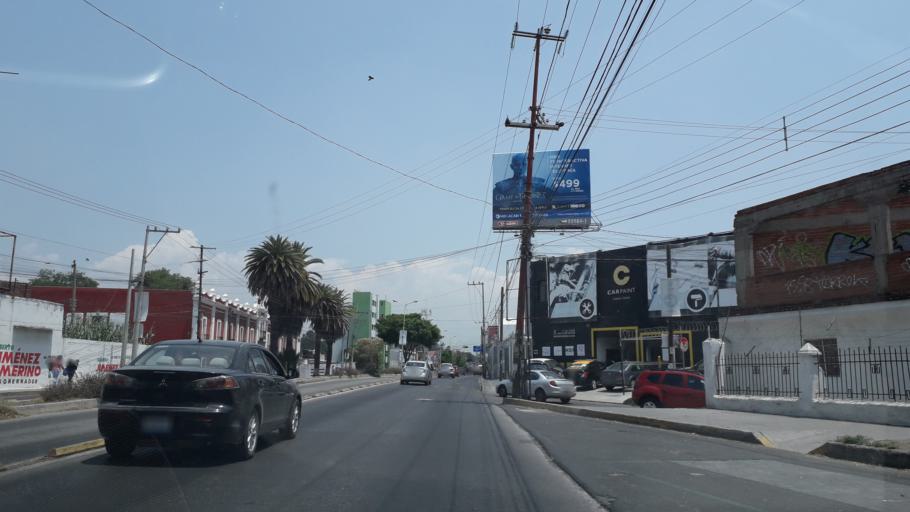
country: MX
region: Puebla
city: Puebla
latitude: 19.0226
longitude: -98.2250
